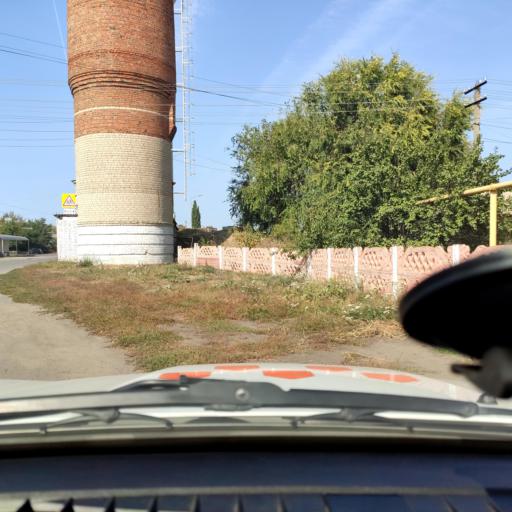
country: RU
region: Voronezj
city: Novaya Usman'
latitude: 51.6532
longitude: 39.3354
